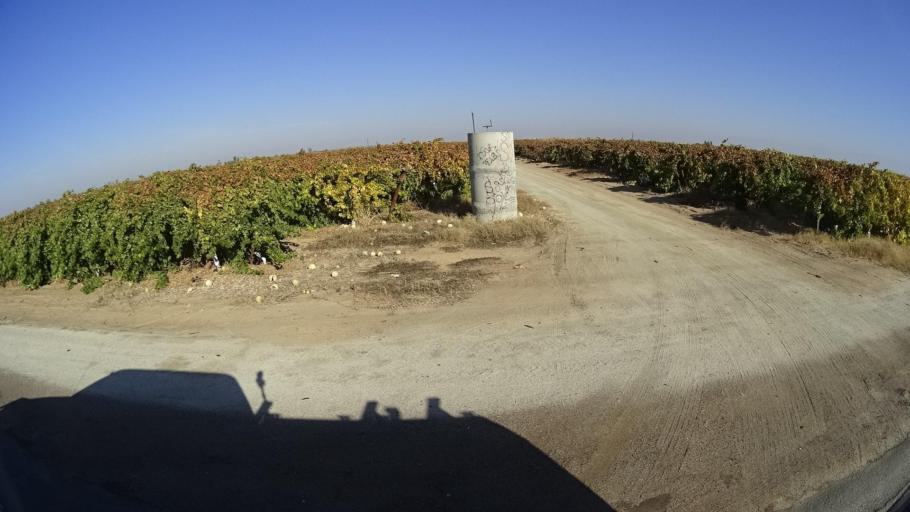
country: US
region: California
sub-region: Kern County
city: Delano
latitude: 35.7469
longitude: -119.1985
